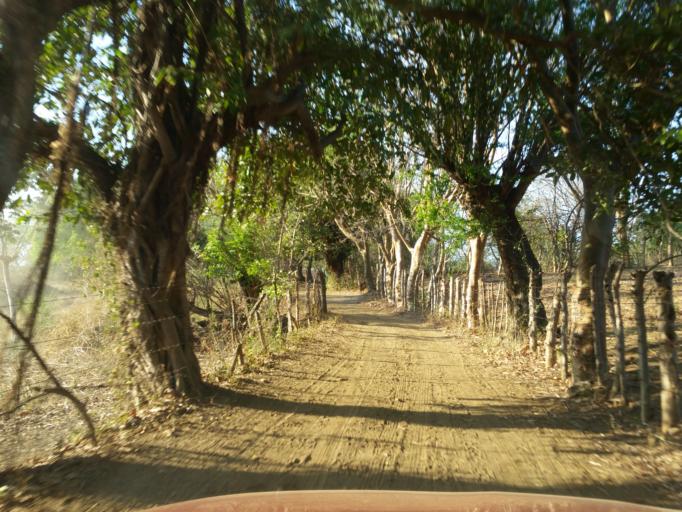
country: NI
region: Managua
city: Managua
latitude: 12.0747
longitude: -86.2583
